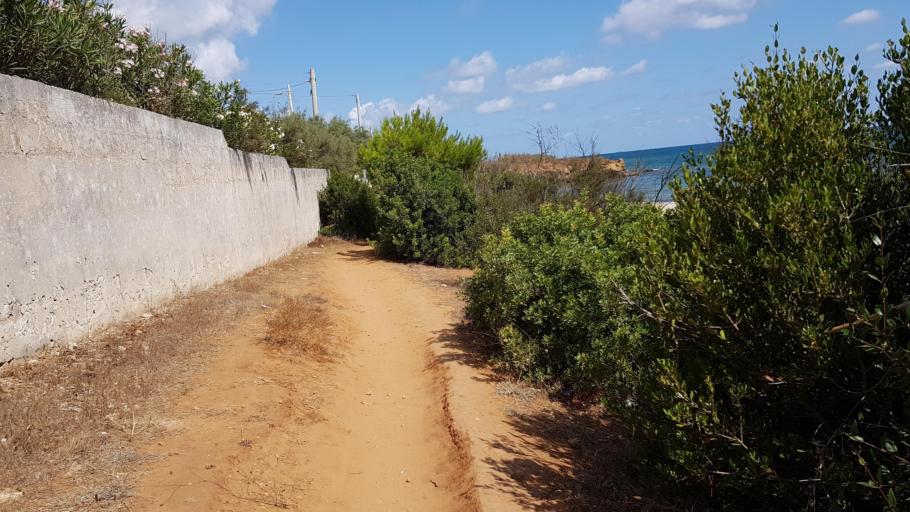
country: IT
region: Apulia
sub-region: Provincia di Brindisi
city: Torchiarolo
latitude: 40.5275
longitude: 18.0787
